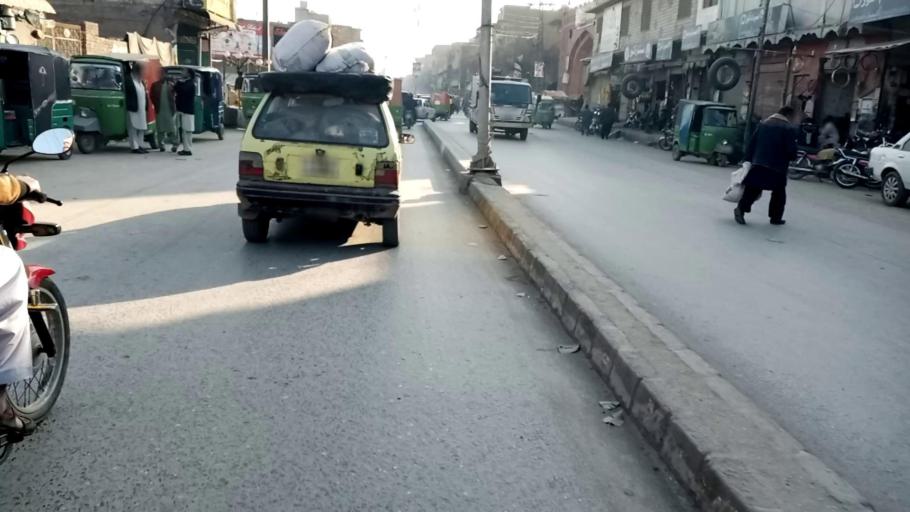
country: PK
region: Khyber Pakhtunkhwa
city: Peshawar
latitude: 34.0109
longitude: 71.5855
